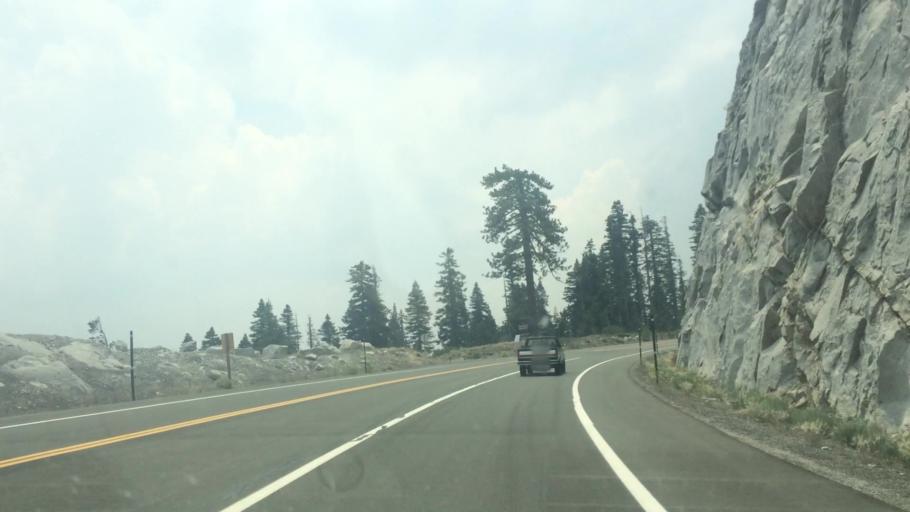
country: US
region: California
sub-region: El Dorado County
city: South Lake Tahoe
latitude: 38.6506
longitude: -120.1315
